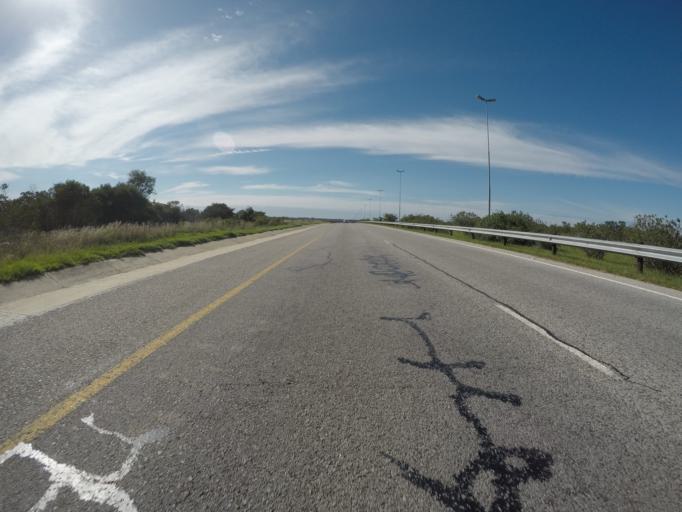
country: ZA
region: Eastern Cape
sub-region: Nelson Mandela Bay Metropolitan Municipality
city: Port Elizabeth
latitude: -33.9482
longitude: 25.4510
